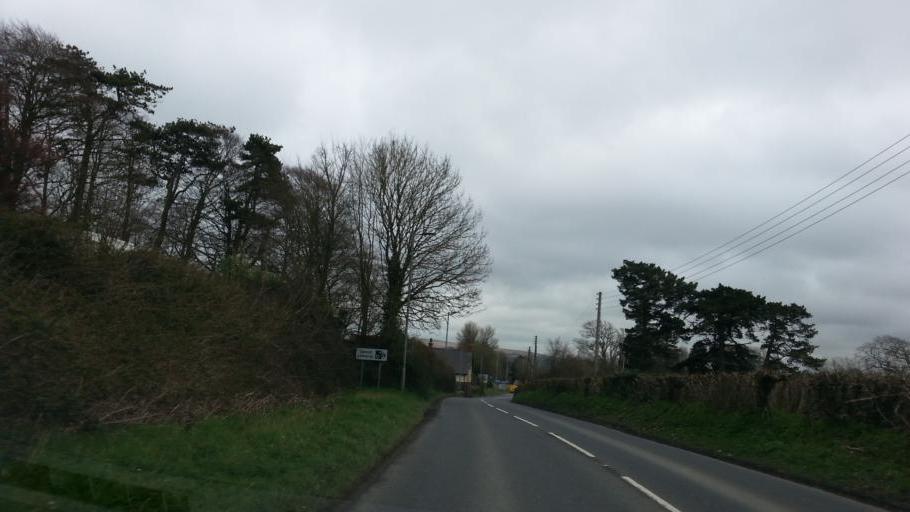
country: GB
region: England
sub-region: Devon
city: Barnstaple
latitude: 51.0956
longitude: -4.0556
